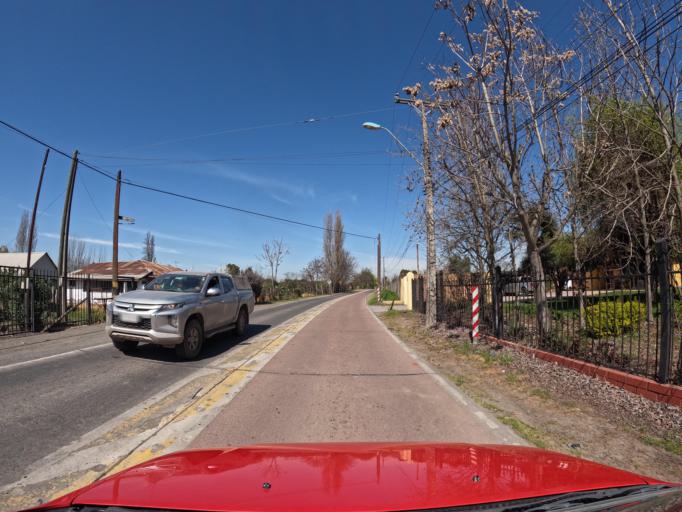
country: CL
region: Maule
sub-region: Provincia de Curico
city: Curico
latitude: -35.0147
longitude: -71.3118
